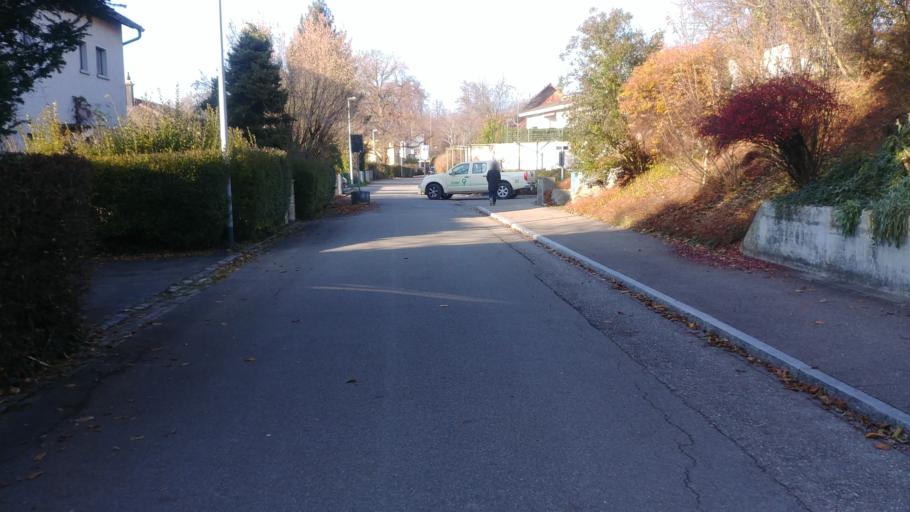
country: CH
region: Zurich
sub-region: Bezirk Uster
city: Uster / Ober-Uster
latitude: 47.3534
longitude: 8.7269
